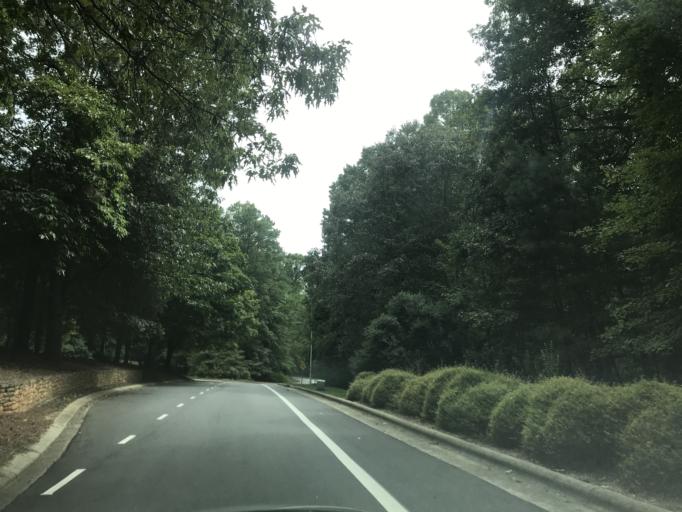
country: US
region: North Carolina
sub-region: Wake County
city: Cary
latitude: 35.7353
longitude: -78.7851
